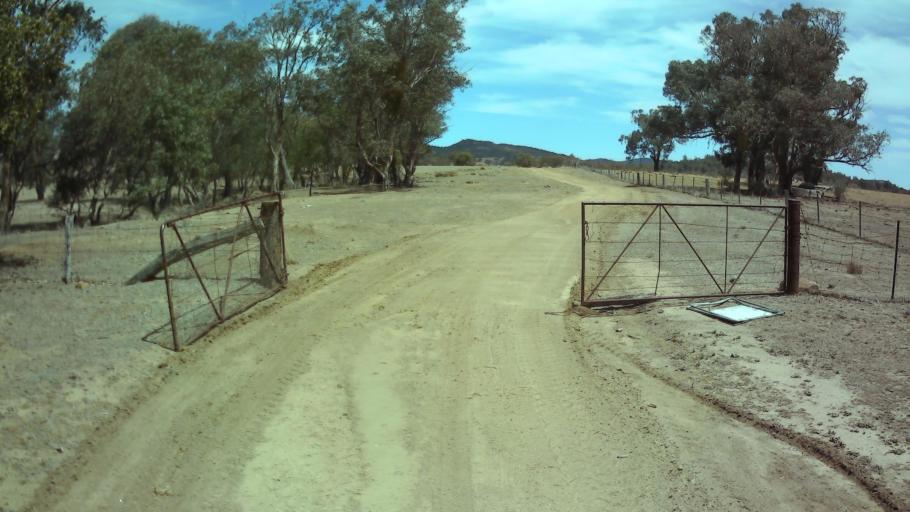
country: AU
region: New South Wales
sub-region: Weddin
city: Grenfell
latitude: -33.7670
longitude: 148.1501
